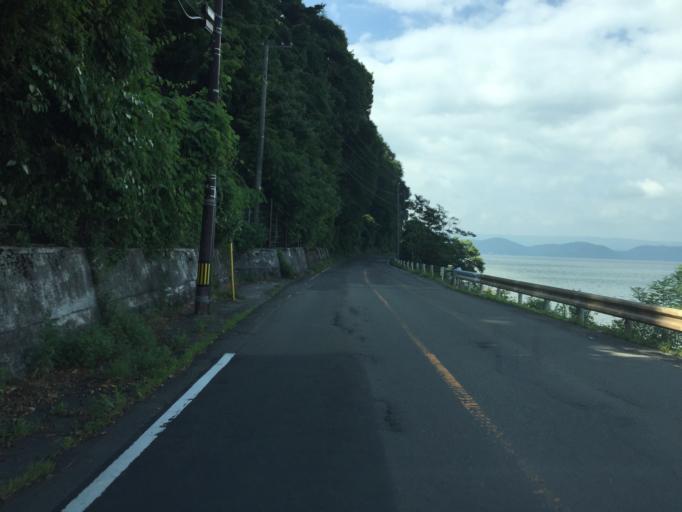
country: JP
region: Fukushima
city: Inawashiro
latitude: 37.4589
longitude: 140.1533
